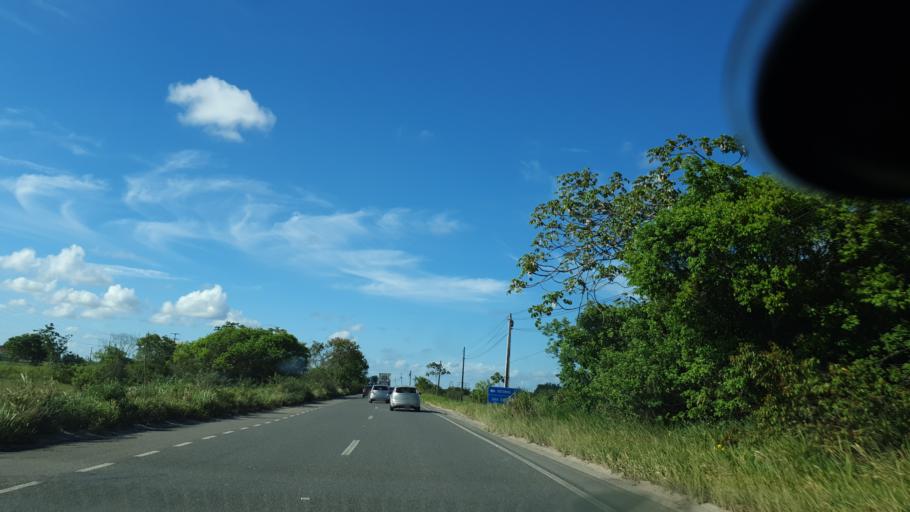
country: BR
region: Bahia
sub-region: Camacari
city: Camacari
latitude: -12.6702
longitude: -38.2998
